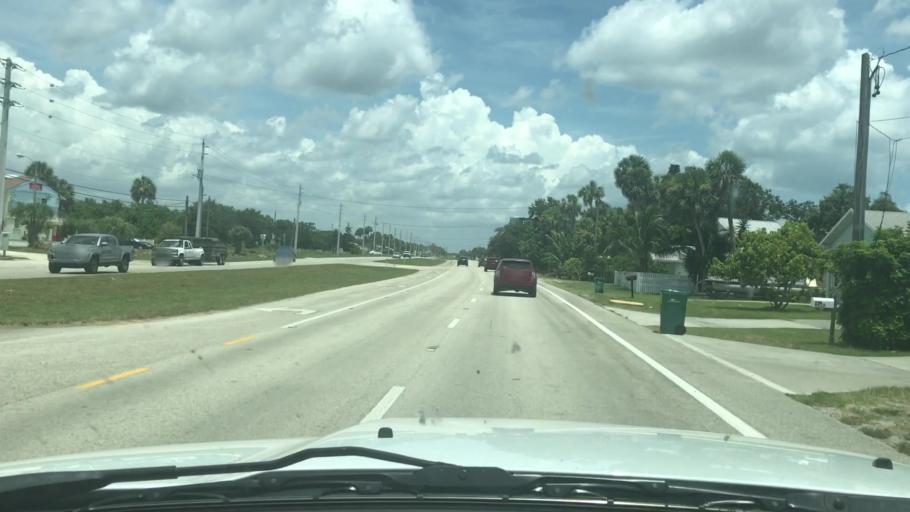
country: US
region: Florida
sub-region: Brevard County
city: Micco
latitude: 27.8667
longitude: -80.4941
